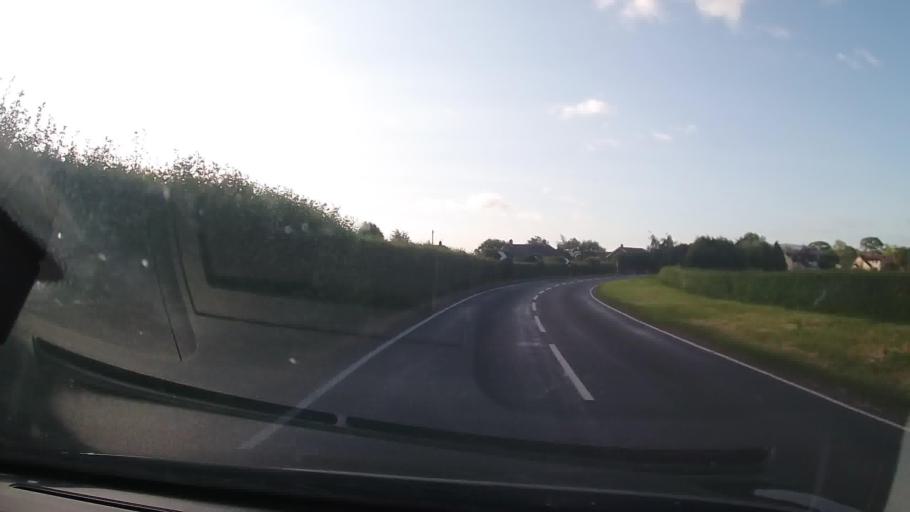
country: GB
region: England
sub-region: Shropshire
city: Withington
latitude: 52.7403
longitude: -2.5735
